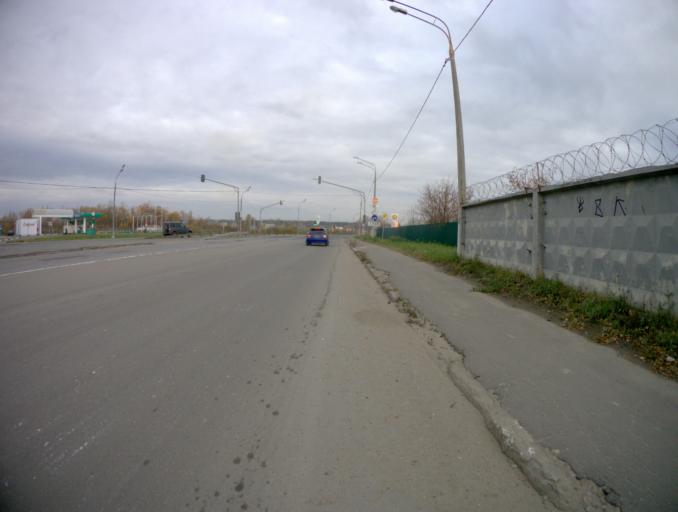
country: RU
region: Moskovskaya
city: Orekhovo-Zuyevo
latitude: 55.8374
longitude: 38.9716
